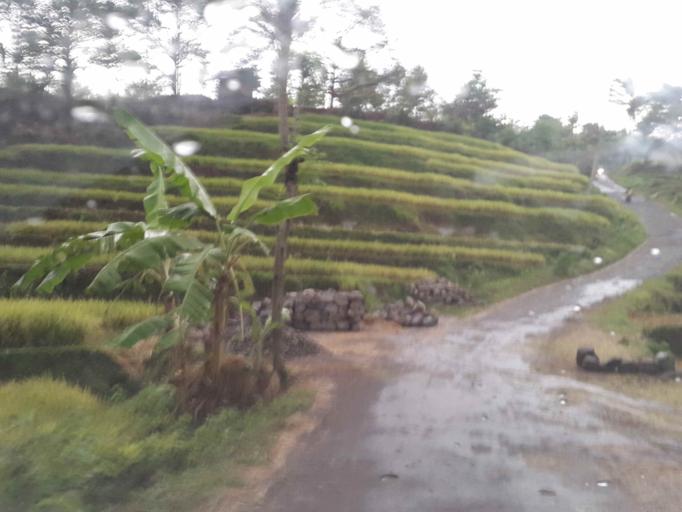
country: ID
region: Central Java
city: Sragen
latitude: -7.5515
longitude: 111.0637
